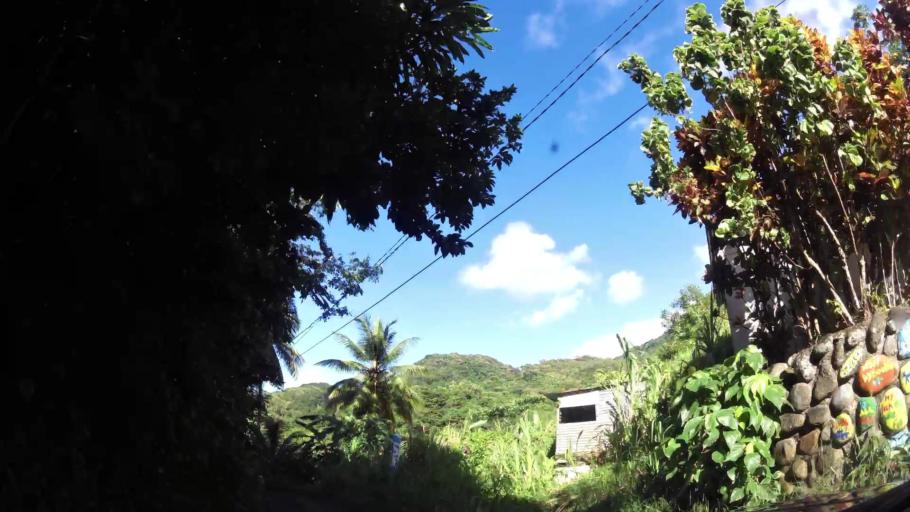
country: DM
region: Saint John
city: Portsmouth
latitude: 15.5800
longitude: -61.4232
